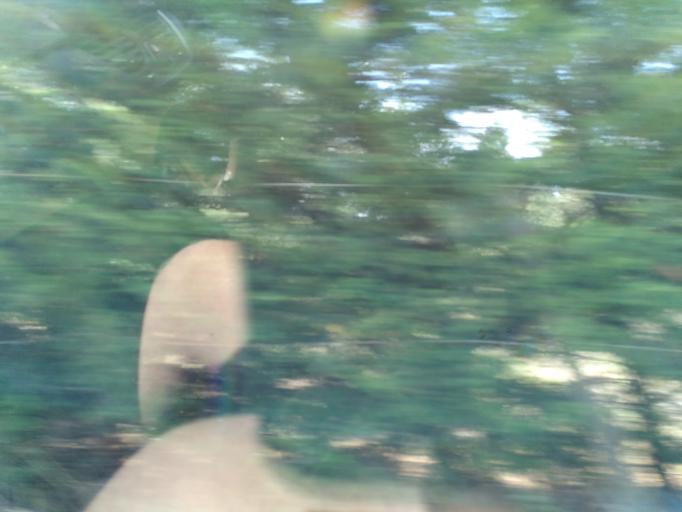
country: GR
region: Central Macedonia
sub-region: Nomos Thessalonikis
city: Agia Triada
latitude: 40.4925
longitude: 22.8624
